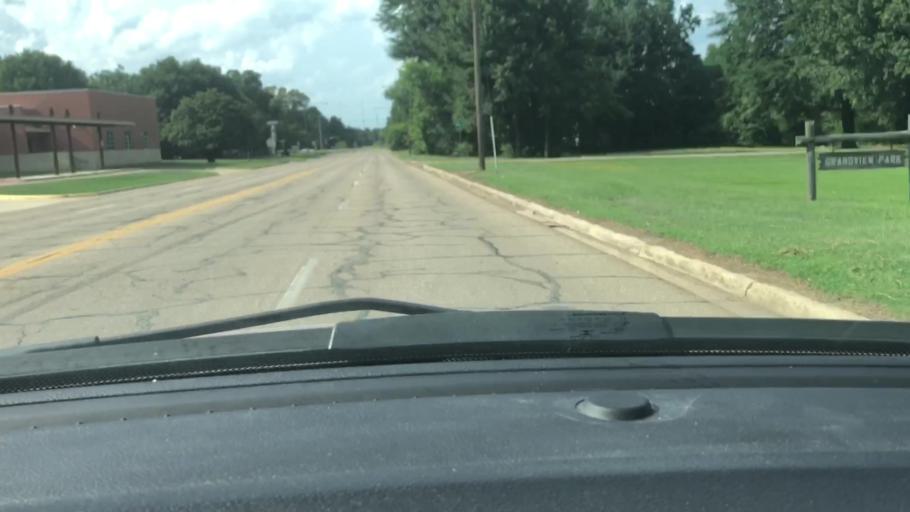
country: US
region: Texas
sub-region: Bowie County
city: Wake Village
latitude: 33.4058
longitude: -94.0790
